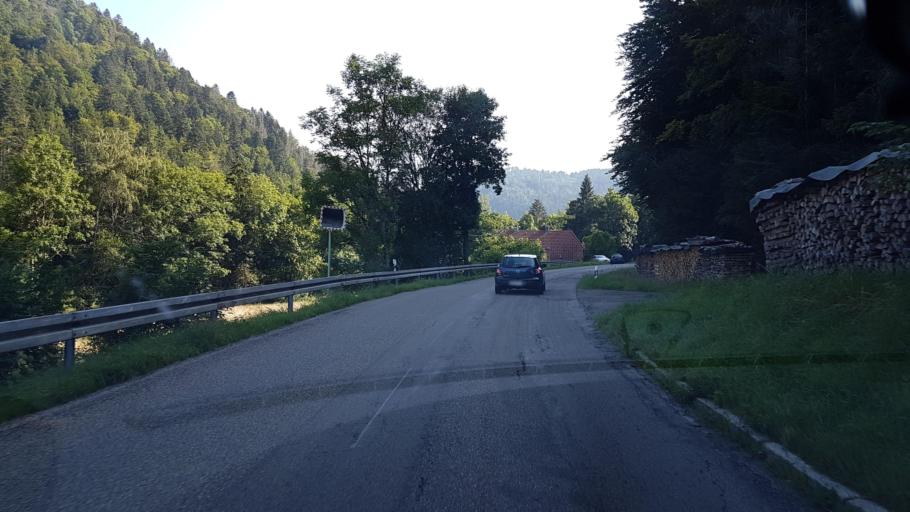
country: DE
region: Baden-Wuerttemberg
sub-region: Freiburg Region
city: Dachsberg
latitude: 47.7200
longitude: 8.1313
